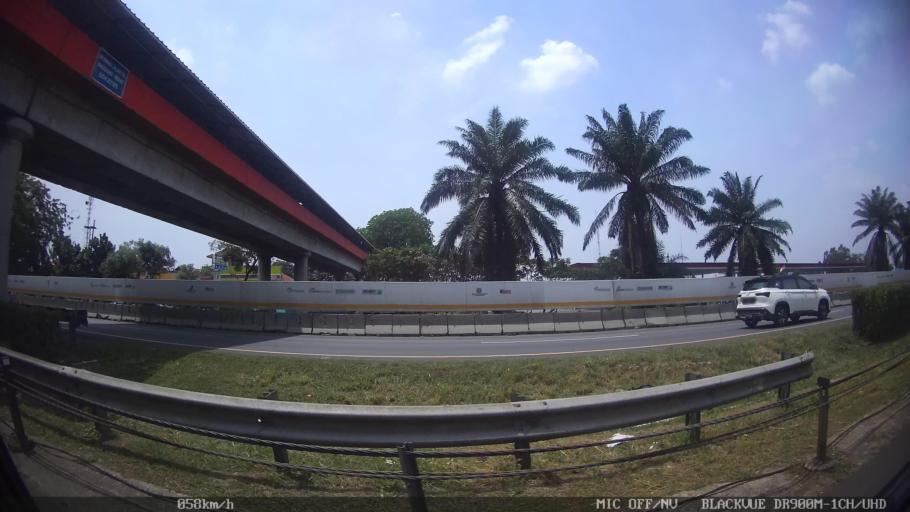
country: ID
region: Banten
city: Serang
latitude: -6.1326
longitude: 106.2054
